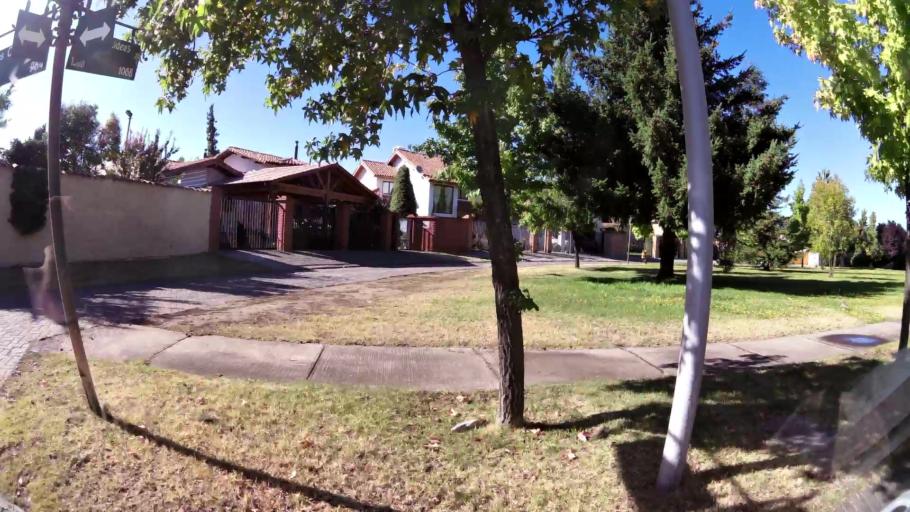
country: CL
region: O'Higgins
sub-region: Provincia de Cachapoal
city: Rancagua
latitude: -34.1902
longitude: -70.7154
